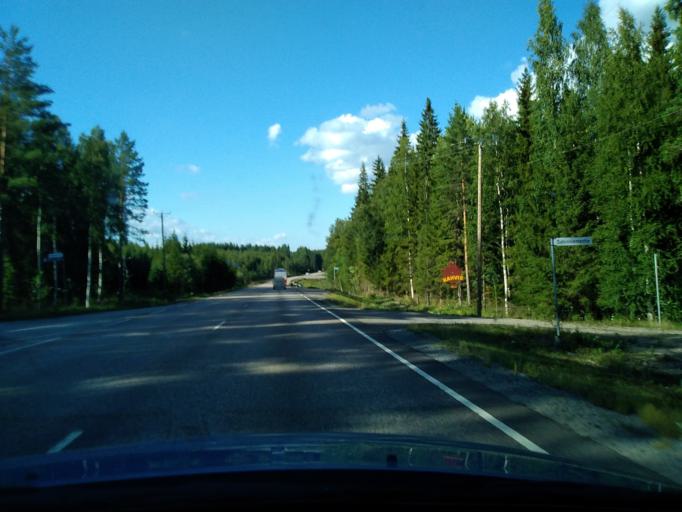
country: FI
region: Pirkanmaa
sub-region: Ylae-Pirkanmaa
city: Maenttae
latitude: 62.0912
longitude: 24.7281
